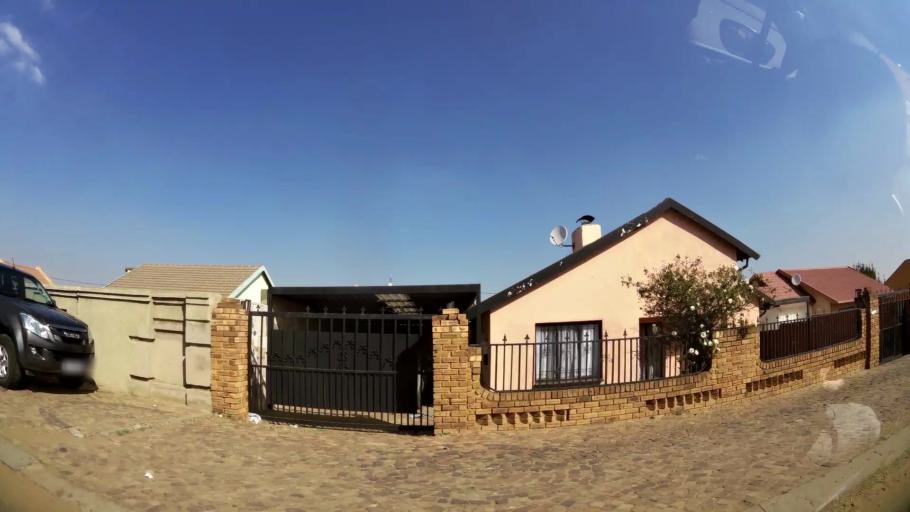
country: ZA
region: Gauteng
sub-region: City of Johannesburg Metropolitan Municipality
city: Roodepoort
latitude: -26.1677
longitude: 27.7952
